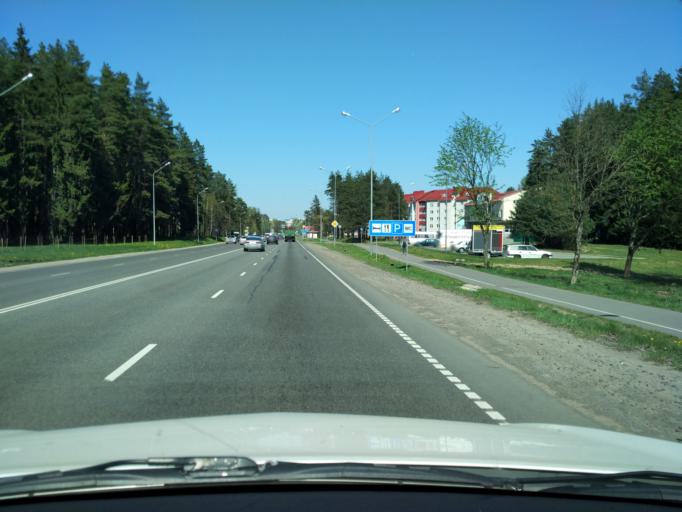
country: BY
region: Minsk
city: Borovlyany
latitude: 53.9869
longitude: 27.6624
